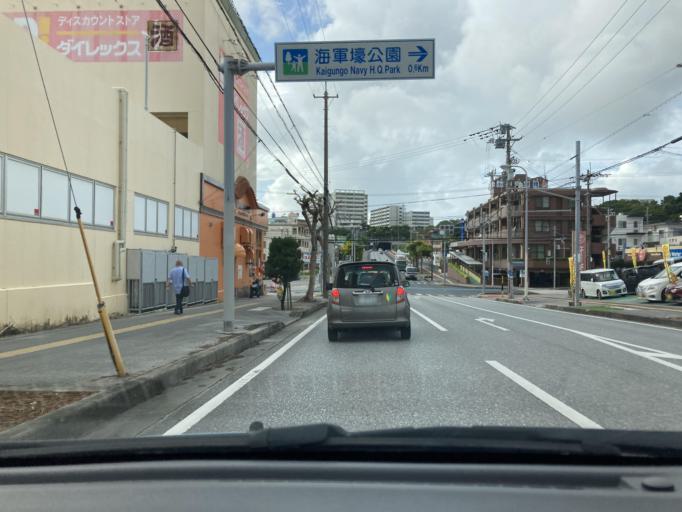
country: JP
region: Okinawa
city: Tomigusuku
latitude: 26.1836
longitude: 127.6767
